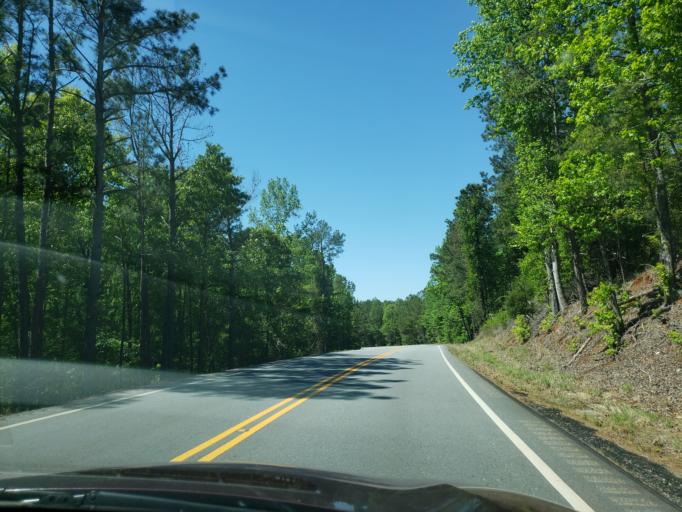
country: US
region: Alabama
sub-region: Tallapoosa County
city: Dadeville
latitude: 32.6703
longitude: -85.7928
